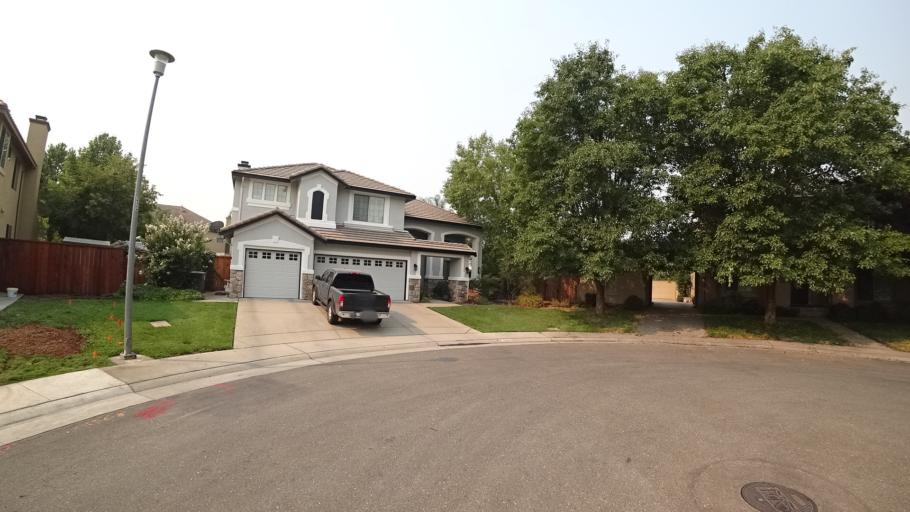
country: US
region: California
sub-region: Sacramento County
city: Laguna
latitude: 38.3973
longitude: -121.4255
